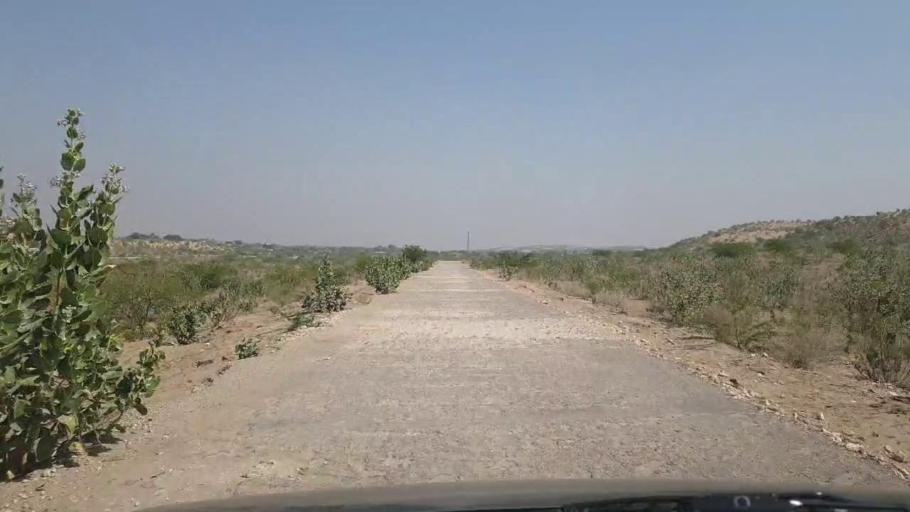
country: PK
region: Sindh
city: Chor
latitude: 25.6896
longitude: 70.1865
